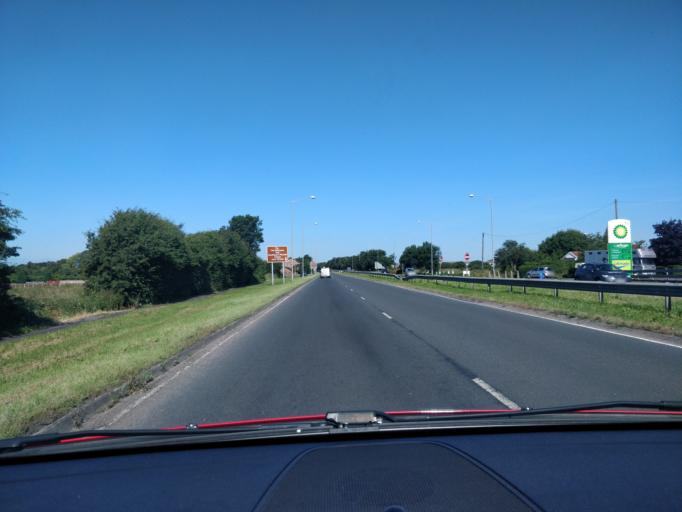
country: GB
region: England
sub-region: Lancashire
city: Banks
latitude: 53.6732
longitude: -2.9232
